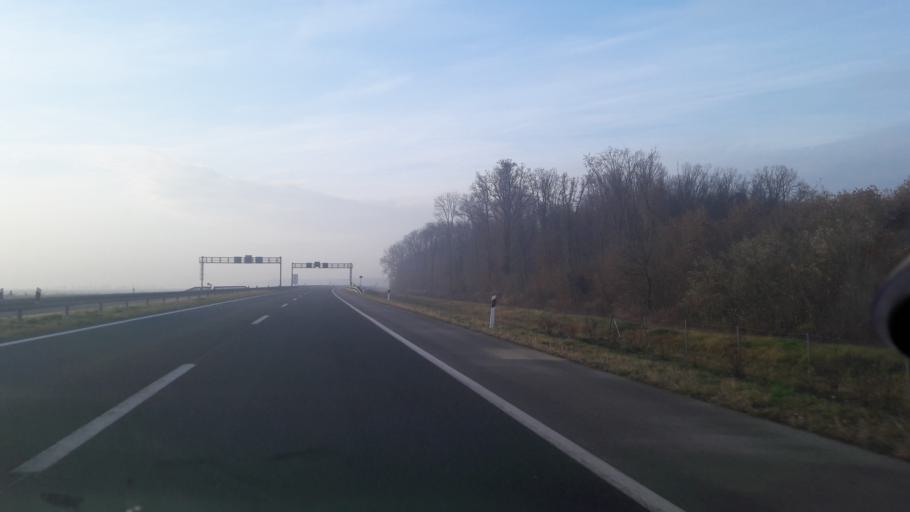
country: HR
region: Osjecko-Baranjska
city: Vuka
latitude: 45.4965
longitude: 18.5027
